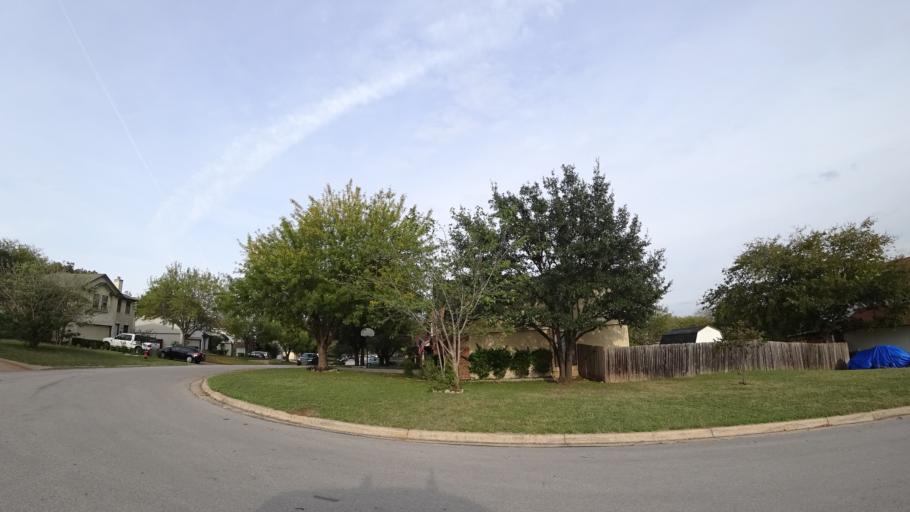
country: US
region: Texas
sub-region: Williamson County
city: Round Rock
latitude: 30.5029
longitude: -97.6636
